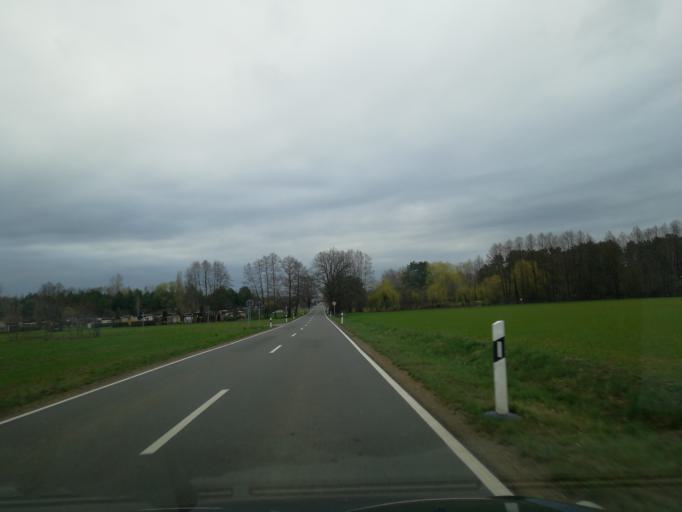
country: DE
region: Brandenburg
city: Vetschau
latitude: 51.7721
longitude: 14.0677
